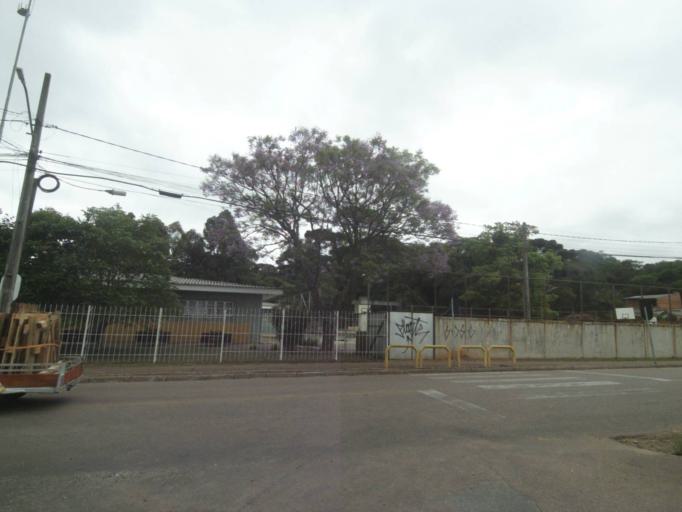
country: BR
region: Parana
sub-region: Sao Jose Dos Pinhais
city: Sao Jose dos Pinhais
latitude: -25.5575
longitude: -49.2571
